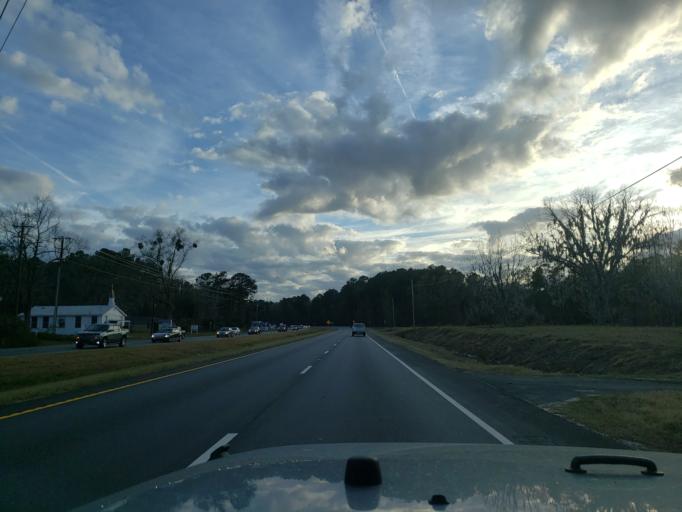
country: US
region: Georgia
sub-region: Chatham County
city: Port Wentworth
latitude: 32.2126
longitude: -81.2001
